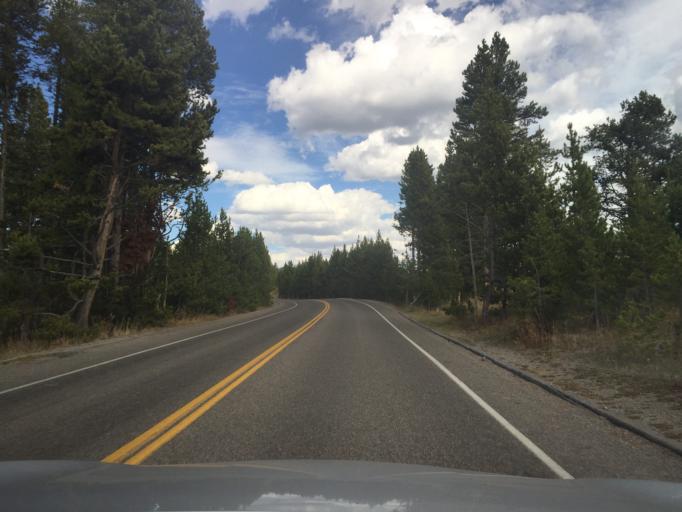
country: US
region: Montana
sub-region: Gallatin County
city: West Yellowstone
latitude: 44.7110
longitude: -110.4987
